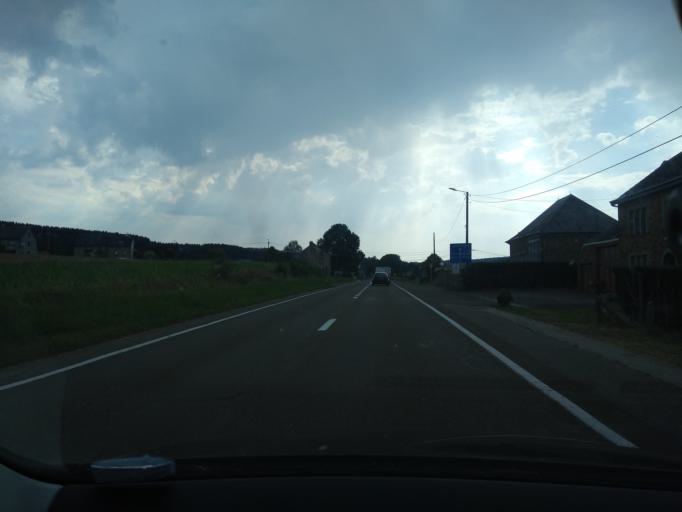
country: BE
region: Wallonia
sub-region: Province du Luxembourg
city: Sainte-Ode
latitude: 50.0253
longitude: 5.5174
